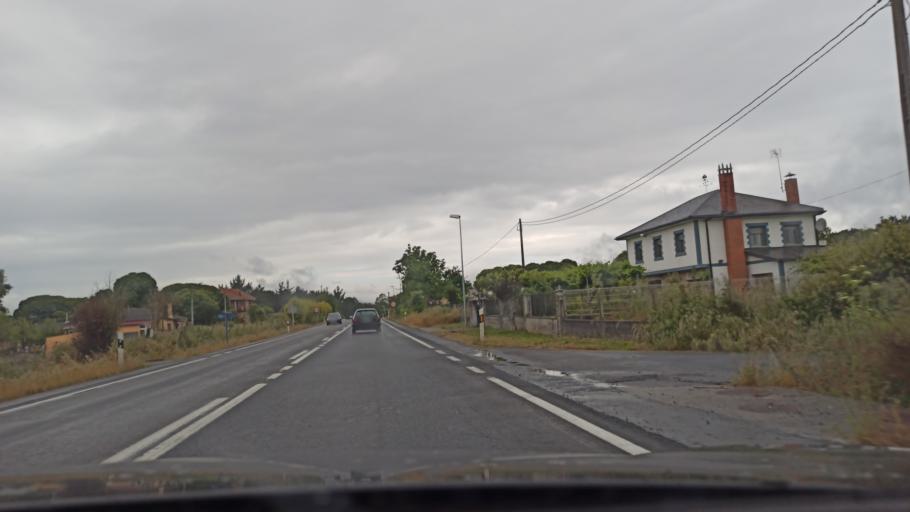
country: ES
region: Galicia
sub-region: Provincia de Lugo
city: Monterroso
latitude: 42.7984
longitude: -7.8026
